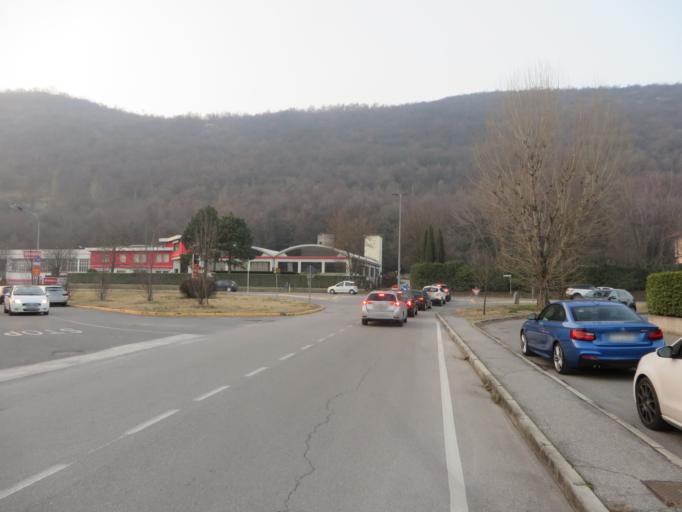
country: IT
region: Lombardy
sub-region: Provincia di Brescia
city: Prevalle
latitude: 45.5637
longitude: 10.4311
